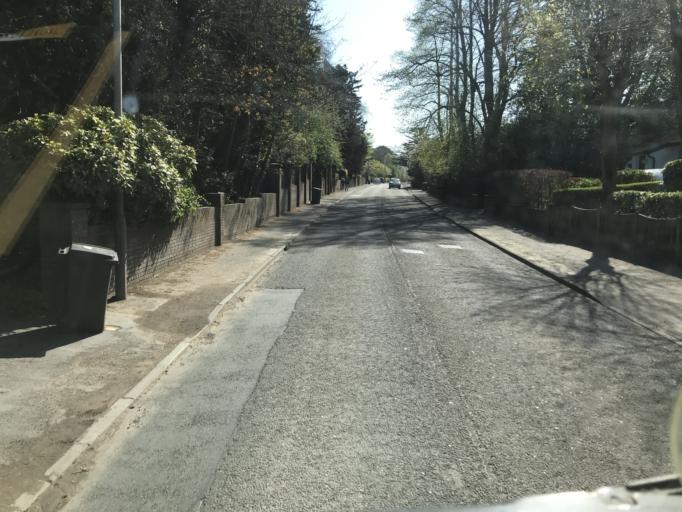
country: GB
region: England
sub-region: Cheshire East
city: Middlewich
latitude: 53.1961
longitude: -2.4580
